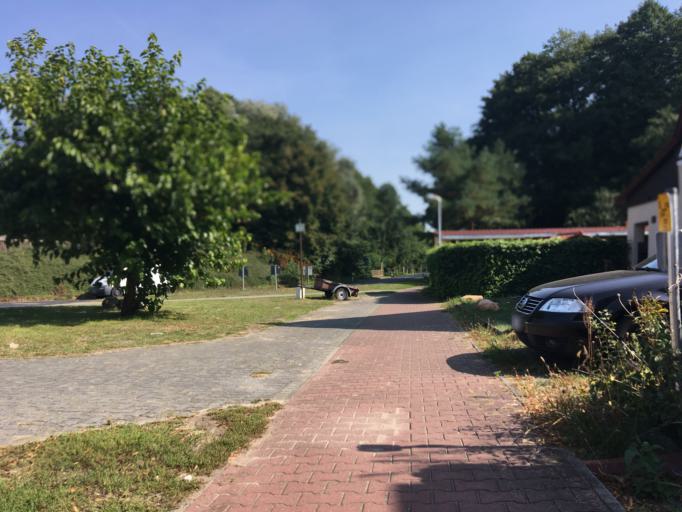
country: DE
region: Brandenburg
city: Erkner
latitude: 52.3934
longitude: 13.7198
